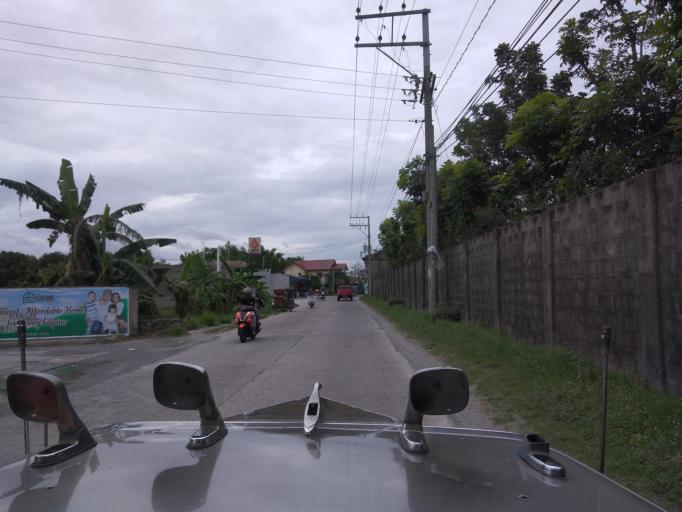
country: PH
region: Central Luzon
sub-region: Province of Pampanga
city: Pandacaqui
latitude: 15.1873
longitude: 120.6392
